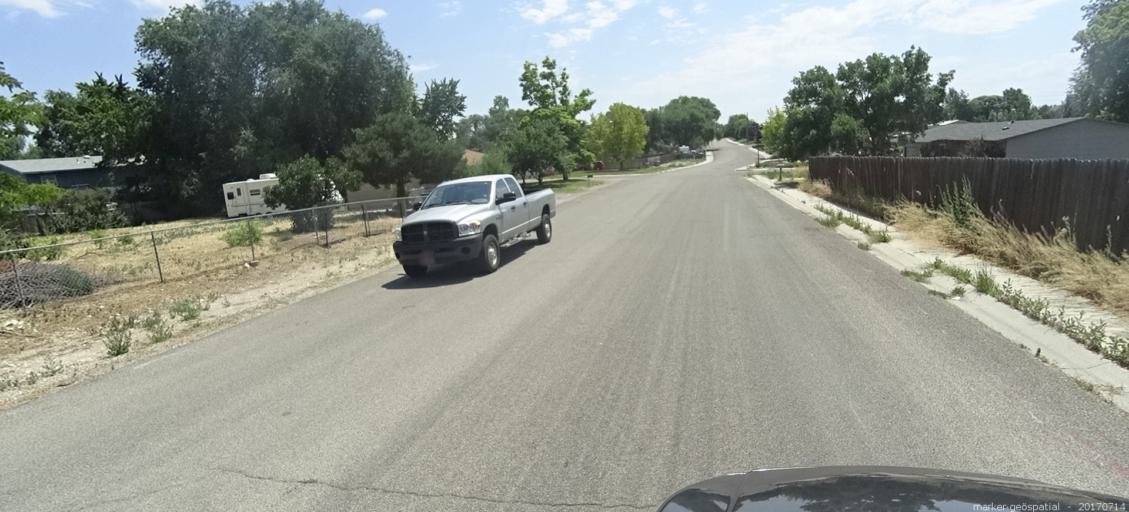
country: US
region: Idaho
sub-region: Ada County
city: Meridian
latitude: 43.5339
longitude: -116.3244
